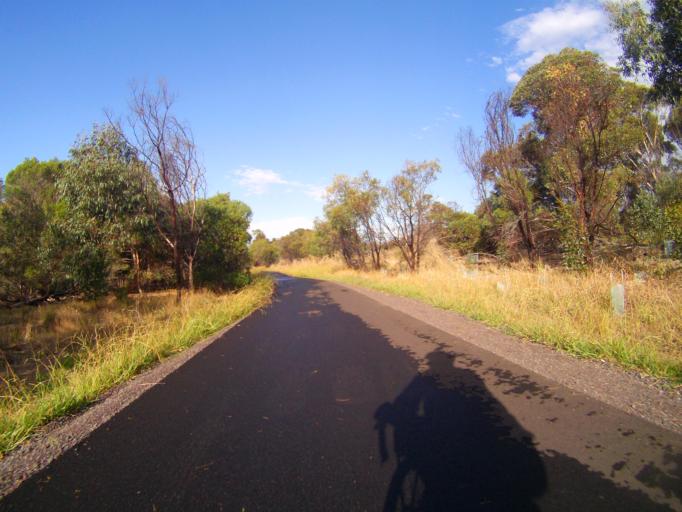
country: AU
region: Victoria
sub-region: Greater Geelong
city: Clifton Springs
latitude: -38.1800
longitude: 144.5266
